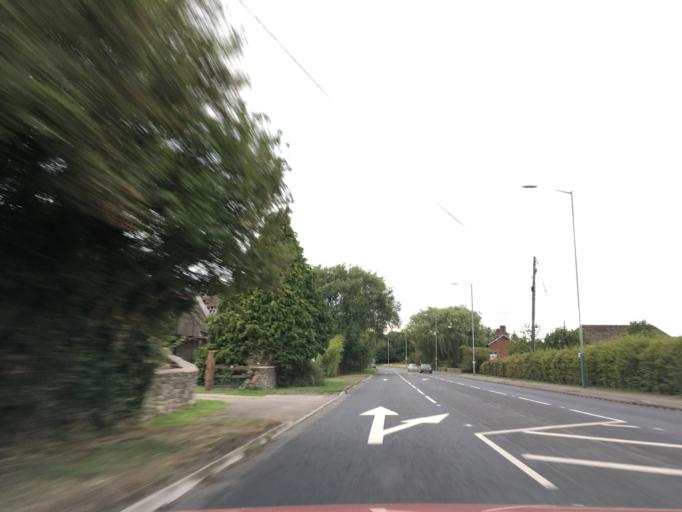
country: GB
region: England
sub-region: Wiltshire
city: Bremhill
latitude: 51.4417
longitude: -2.0766
